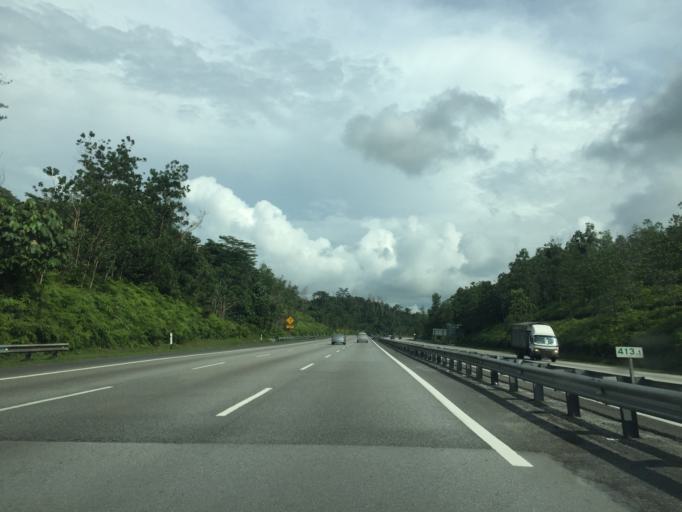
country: MY
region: Selangor
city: Batang Berjuntai
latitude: 3.5503
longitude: 101.5185
